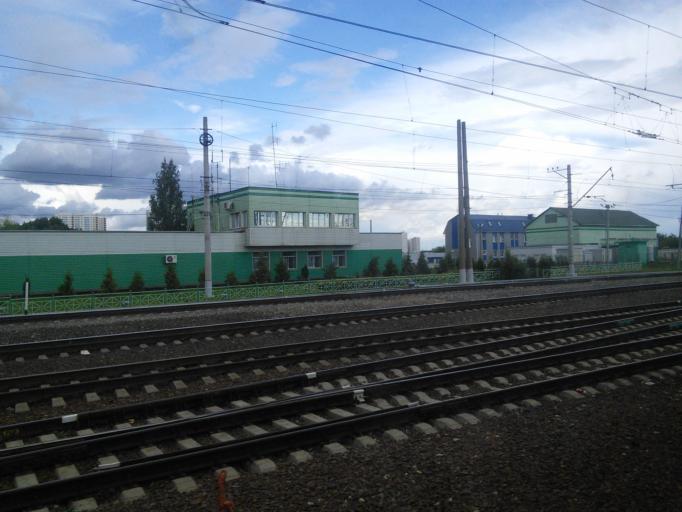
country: RU
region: Moskovskaya
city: Lyubertsy
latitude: 55.6803
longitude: 37.9009
